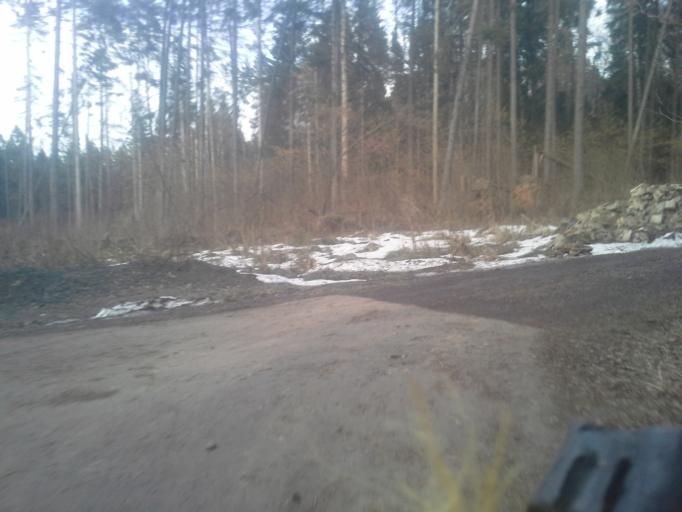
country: RU
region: Moskovskaya
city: Lesnoy Gorodok
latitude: 55.6398
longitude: 37.2401
